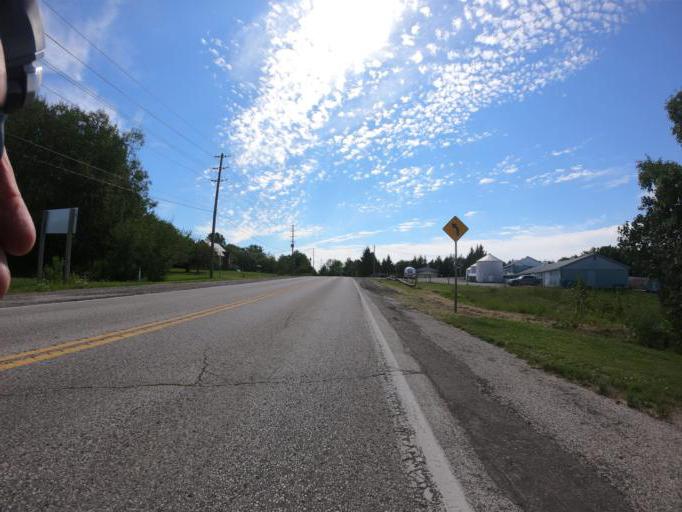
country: CA
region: Ontario
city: Waterloo
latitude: 43.4924
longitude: -80.4499
